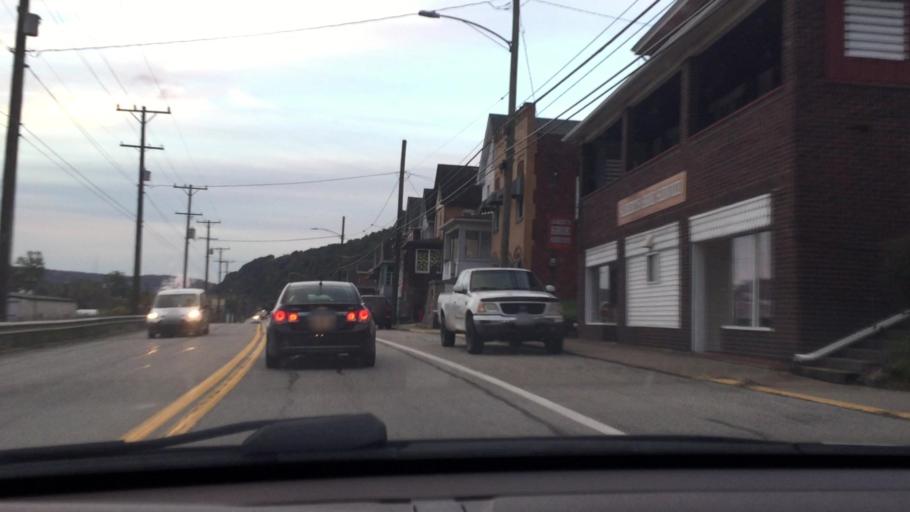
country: US
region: Pennsylvania
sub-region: Westmoreland County
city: Arnold
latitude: 40.5799
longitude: -79.7791
